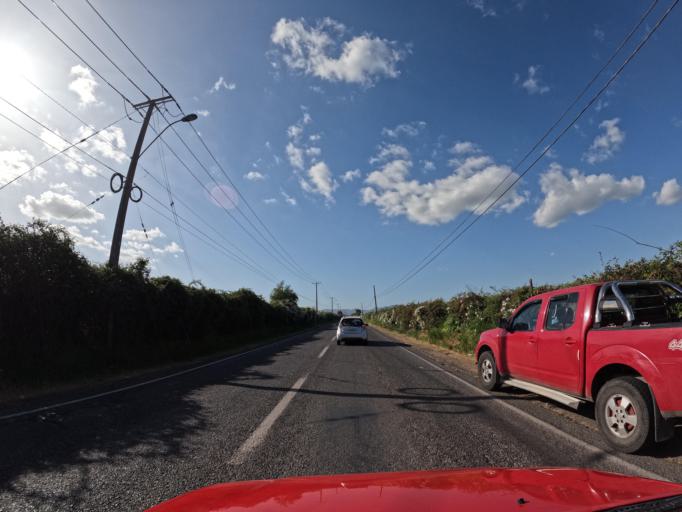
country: CL
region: Maule
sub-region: Provincia de Curico
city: Rauco
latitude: -34.9296
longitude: -71.2766
